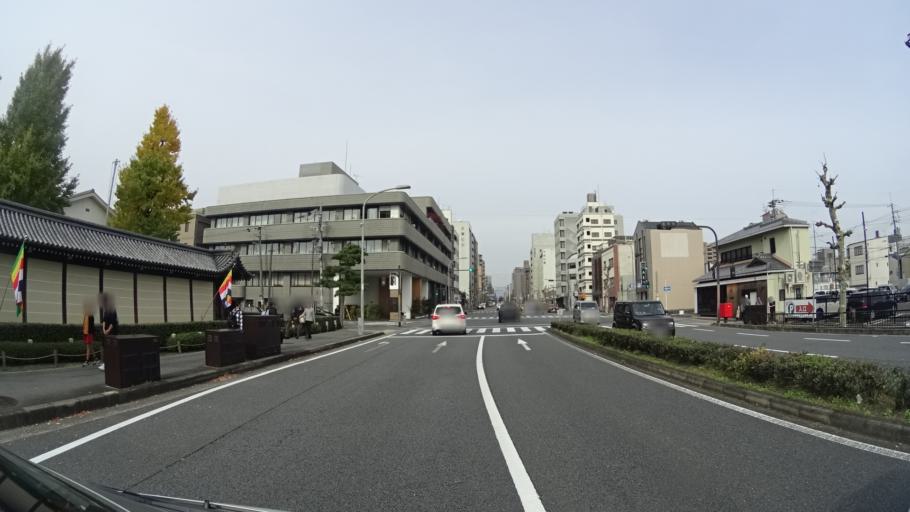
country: JP
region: Kyoto
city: Kyoto
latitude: 34.9928
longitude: 135.7597
